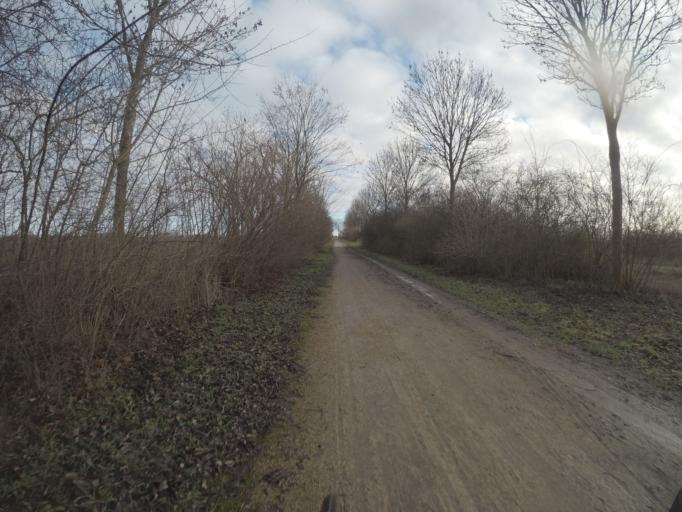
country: DE
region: Berlin
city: Wartenberg
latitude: 52.5924
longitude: 13.5157
